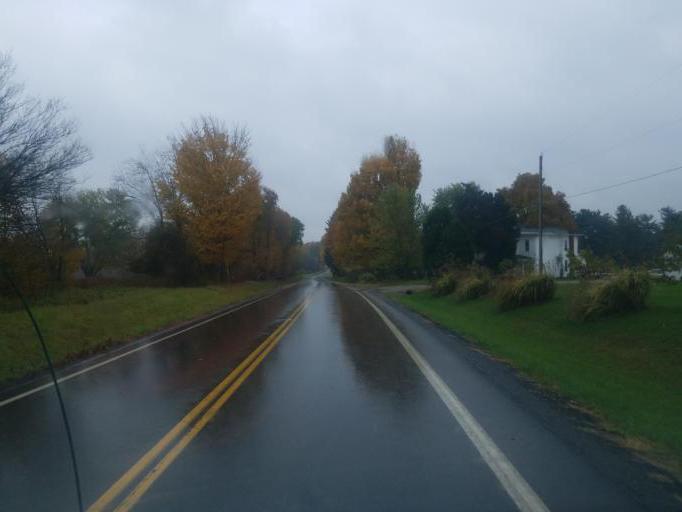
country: US
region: Ohio
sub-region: Licking County
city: Utica
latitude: 40.2741
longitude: -82.3590
